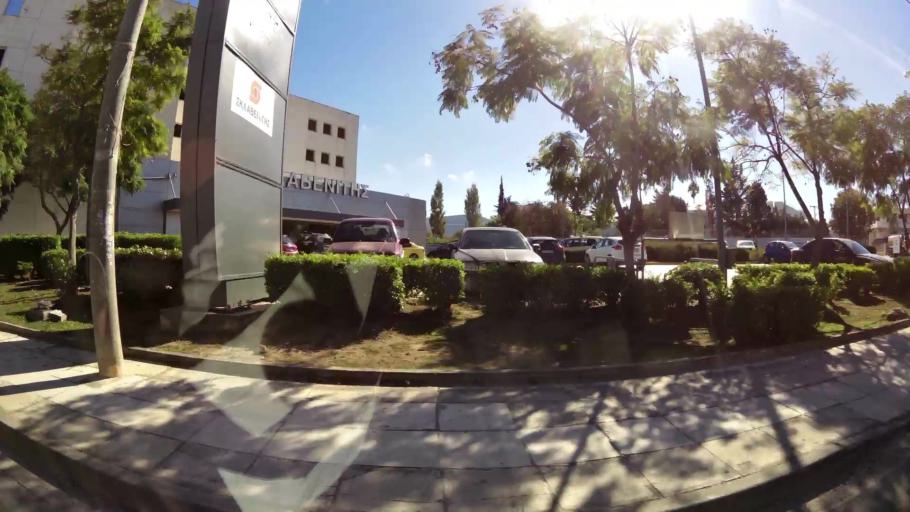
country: GR
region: Attica
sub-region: Nomarchia Anatolikis Attikis
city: Markopoulo
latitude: 37.8875
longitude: 23.9423
